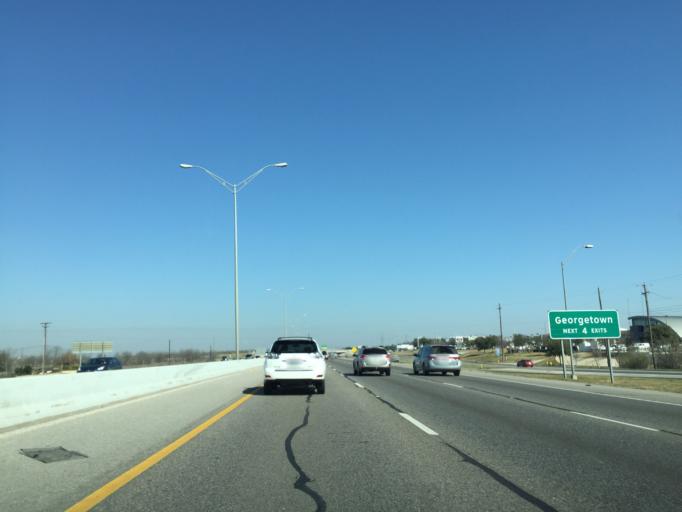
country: US
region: Texas
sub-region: Williamson County
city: Round Rock
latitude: 30.5705
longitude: -97.6927
